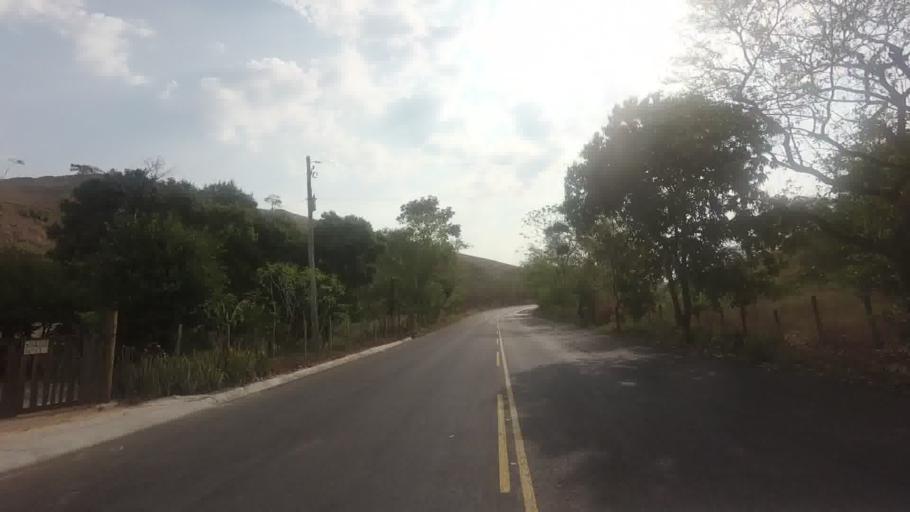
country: BR
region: Rio de Janeiro
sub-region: Itaperuna
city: Itaperuna
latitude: -21.2924
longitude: -41.8174
